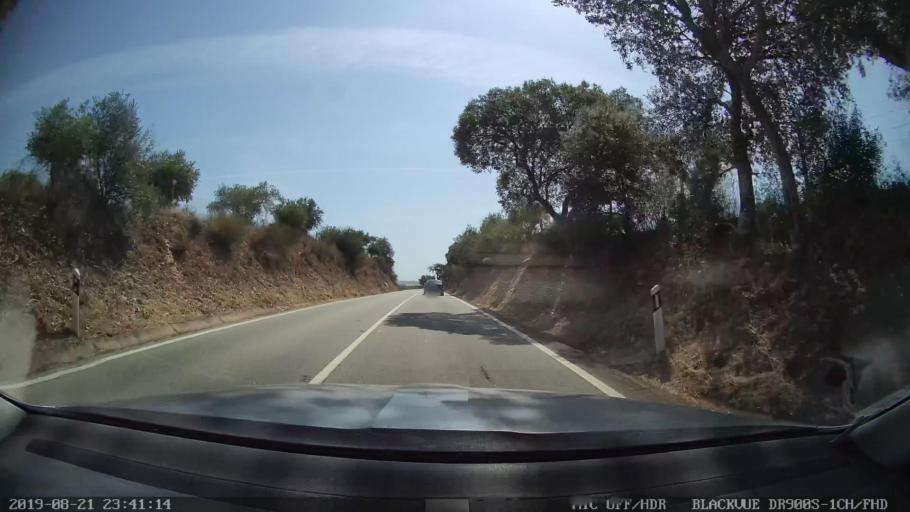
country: PT
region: Castelo Branco
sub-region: Idanha-A-Nova
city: Idanha-a-Nova
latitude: 39.8640
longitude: -7.3249
